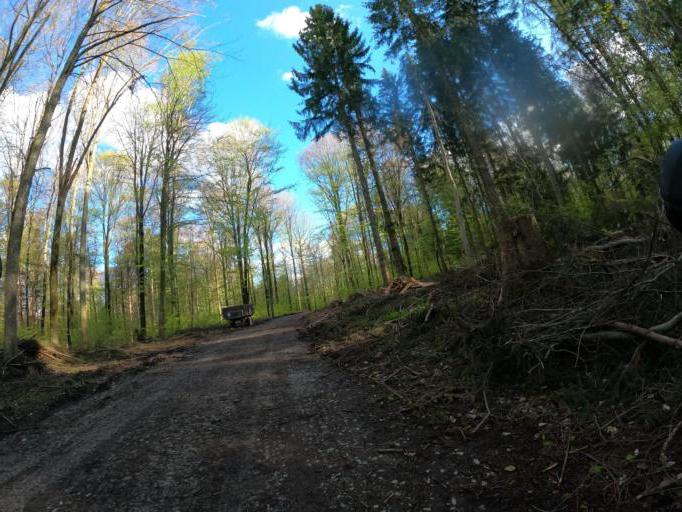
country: DE
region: Baden-Wuerttemberg
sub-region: Karlsruhe Region
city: Gechingen
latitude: 48.6894
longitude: 8.8513
